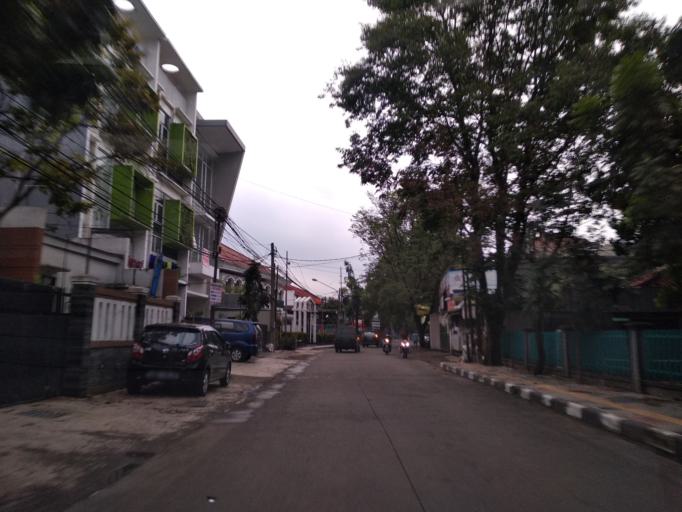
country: ID
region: West Java
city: Bandung
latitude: -6.9414
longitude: 107.6285
